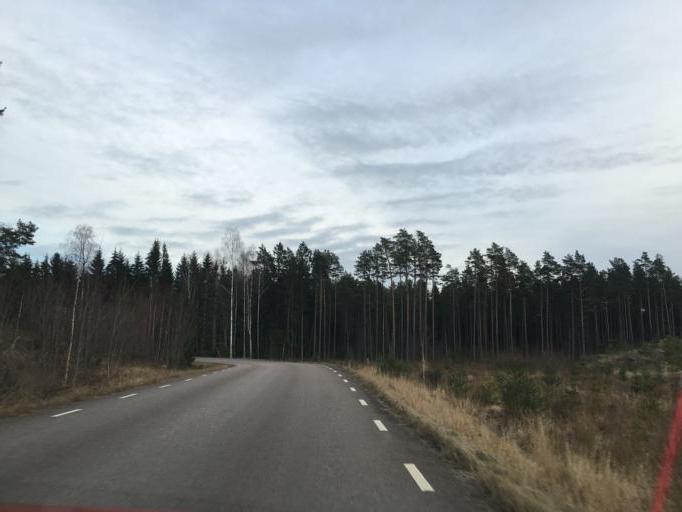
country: SE
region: OEstergoetland
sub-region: Norrkopings Kommun
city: Norrkoping
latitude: 58.4481
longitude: 16.1175
